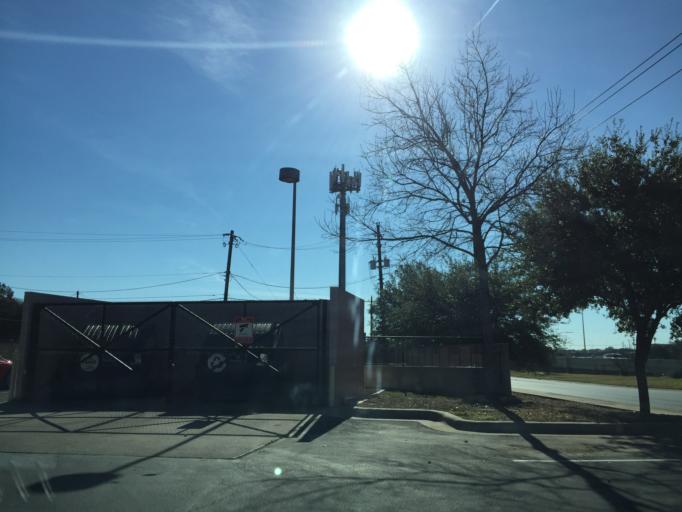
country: US
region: Texas
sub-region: Williamson County
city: Jollyville
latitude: 30.4255
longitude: -97.7505
